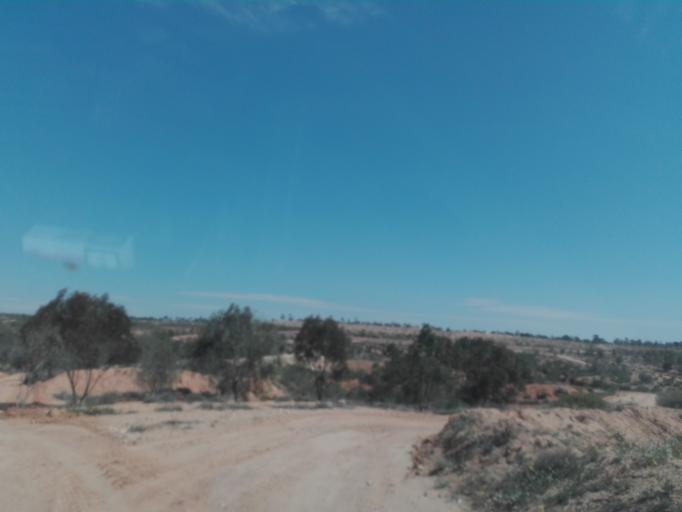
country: TN
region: Safaqis
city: Sfax
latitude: 34.6935
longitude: 10.5302
